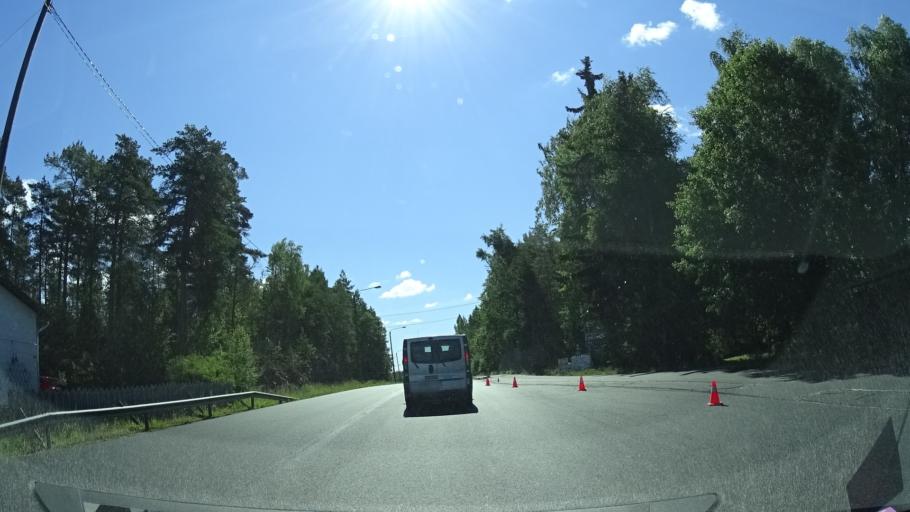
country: FI
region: Varsinais-Suomi
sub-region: Turku
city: Raisio
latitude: 60.5082
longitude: 22.1307
